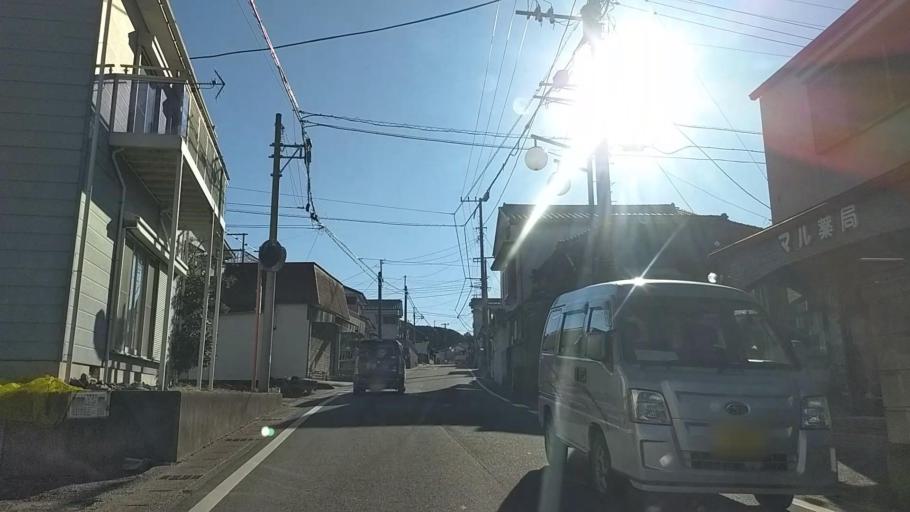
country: JP
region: Chiba
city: Futtsu
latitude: 35.2798
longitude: 139.8556
